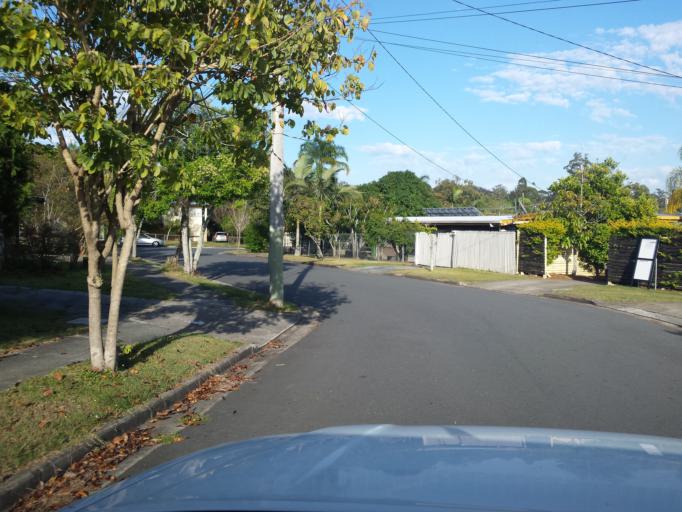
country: AU
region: Queensland
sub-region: Logan
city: Logan City
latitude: -27.6479
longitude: 153.1107
